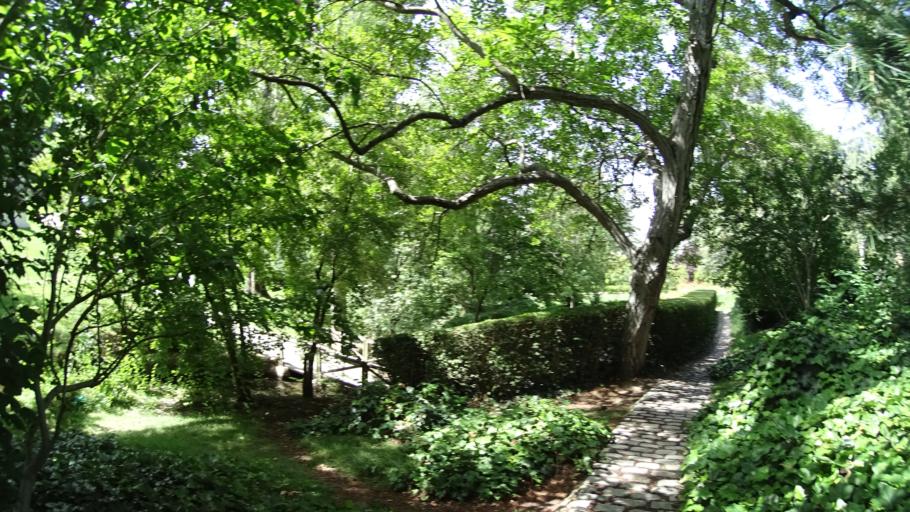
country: ES
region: Madrid
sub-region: Provincia de Madrid
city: Moncloa-Aravaca
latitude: 40.4339
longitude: -3.7274
